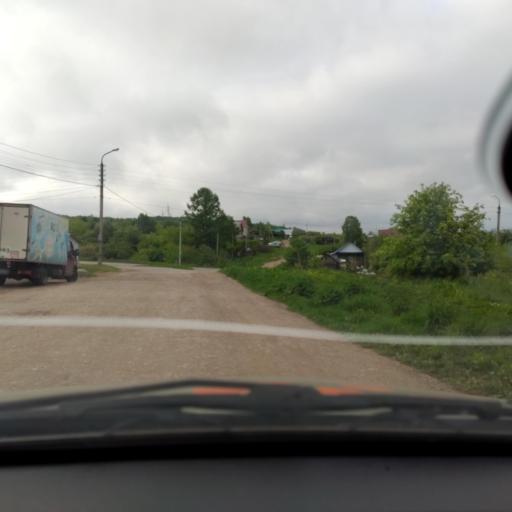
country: RU
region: Bashkortostan
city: Blagoveshchensk
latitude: 54.8902
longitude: 56.0407
